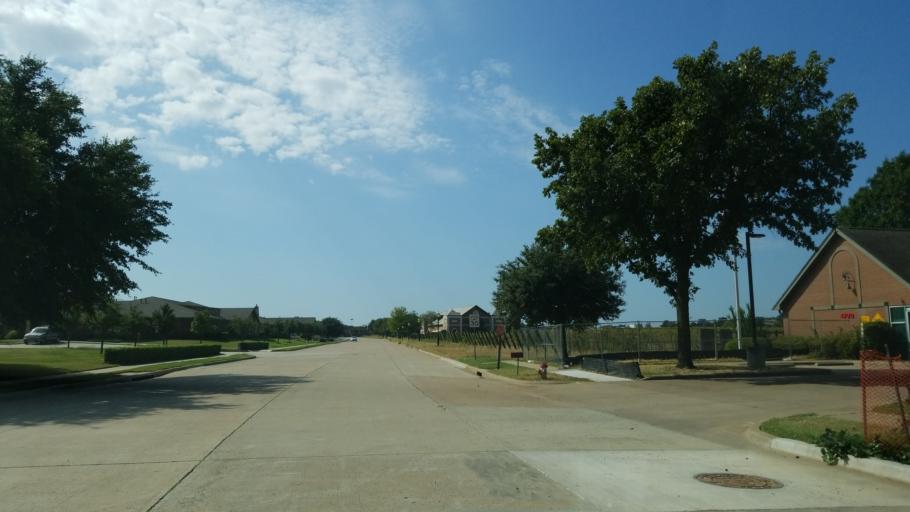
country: US
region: Texas
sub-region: Tarrant County
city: Grapevine
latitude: 32.8886
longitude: -97.0965
